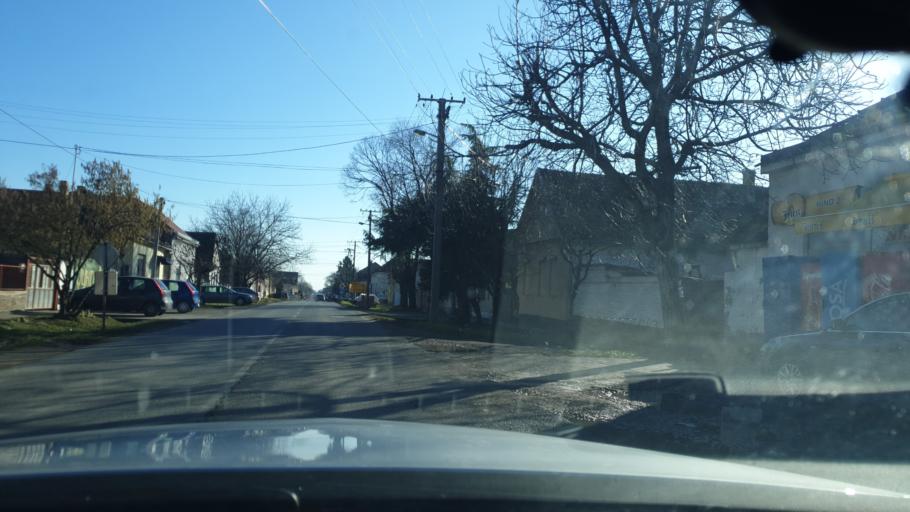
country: RS
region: Autonomna Pokrajina Vojvodina
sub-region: Sremski Okrug
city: Ruma
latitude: 45.0114
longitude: 19.8161
